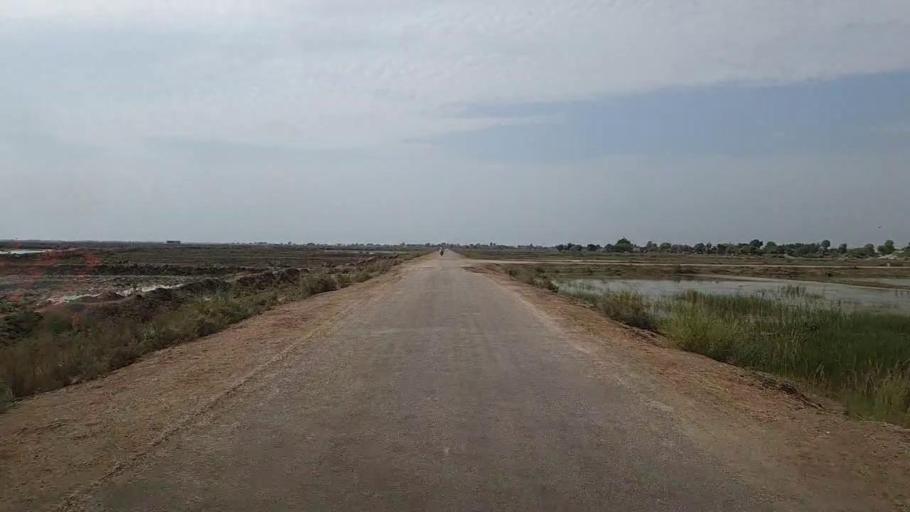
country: PK
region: Sindh
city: Thul
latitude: 28.2896
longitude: 68.8226
